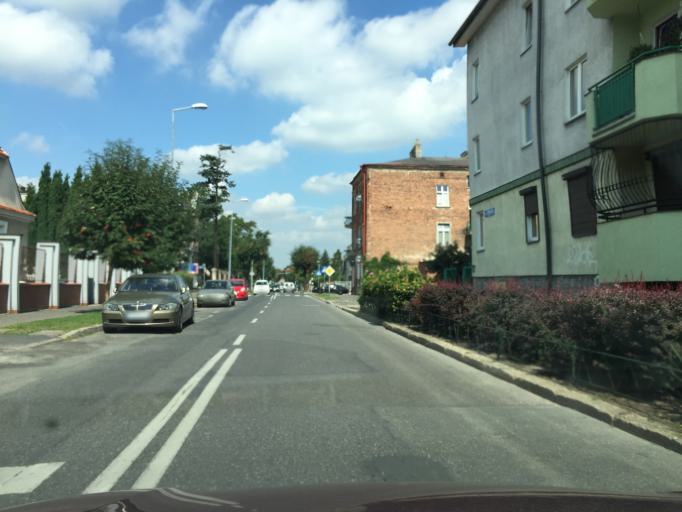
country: PL
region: Greater Poland Voivodeship
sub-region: Kalisz
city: Kalisz
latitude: 51.7560
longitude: 18.0768
